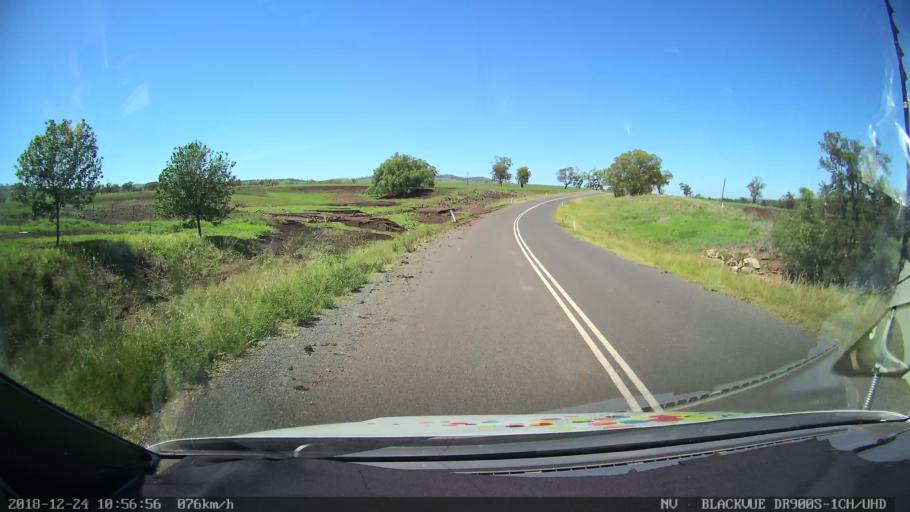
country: AU
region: New South Wales
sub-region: Upper Hunter Shire
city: Merriwa
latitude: -32.0310
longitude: 150.4166
